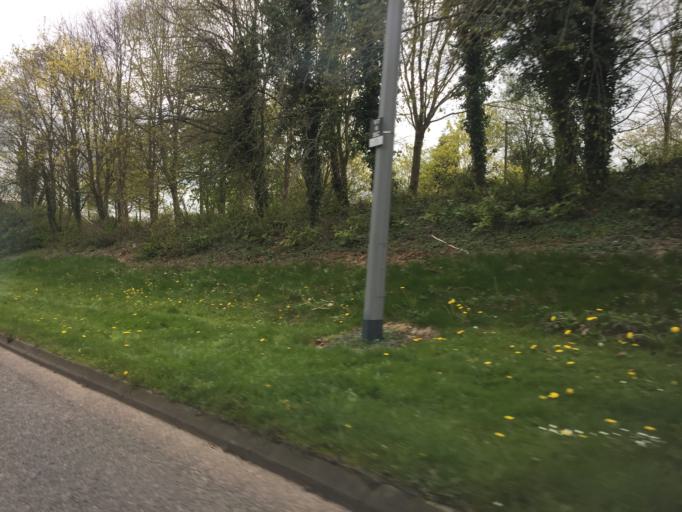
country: GB
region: England
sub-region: Milton Keynes
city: Milton Keynes
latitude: 52.0456
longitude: -0.7646
